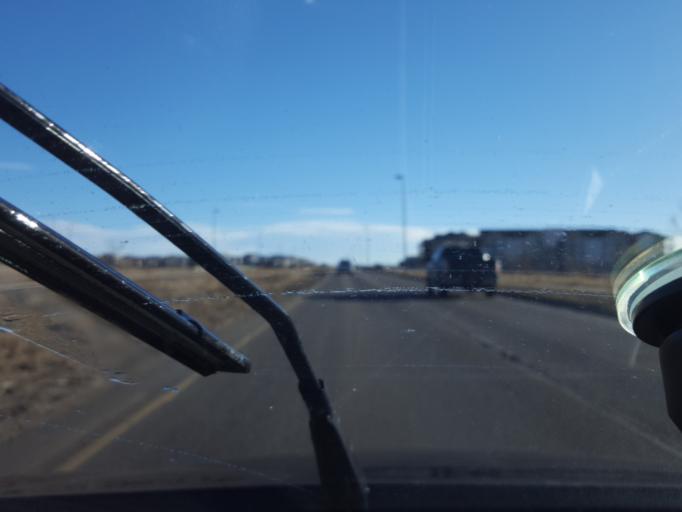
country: US
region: Colorado
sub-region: Adams County
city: Aurora
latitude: 39.7970
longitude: -104.7722
